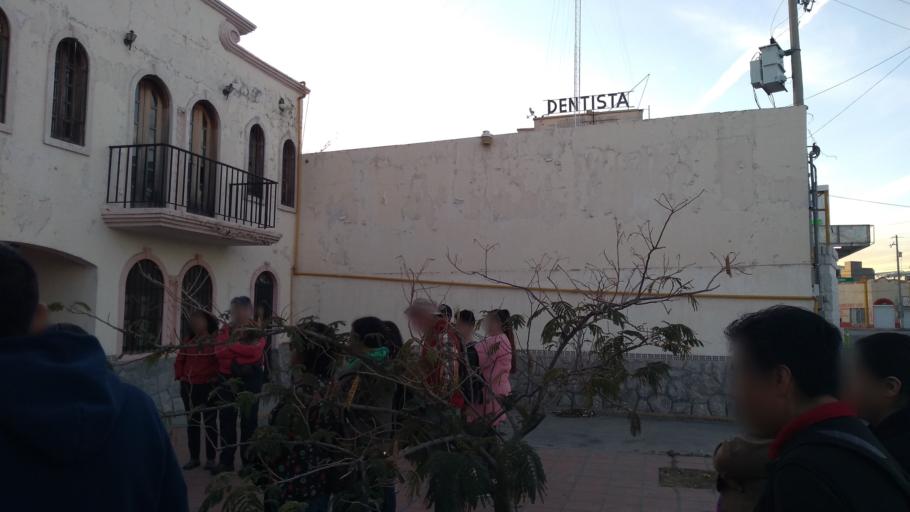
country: MX
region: Chihuahua
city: Ciudad Juarez
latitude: 31.7426
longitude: -106.4807
